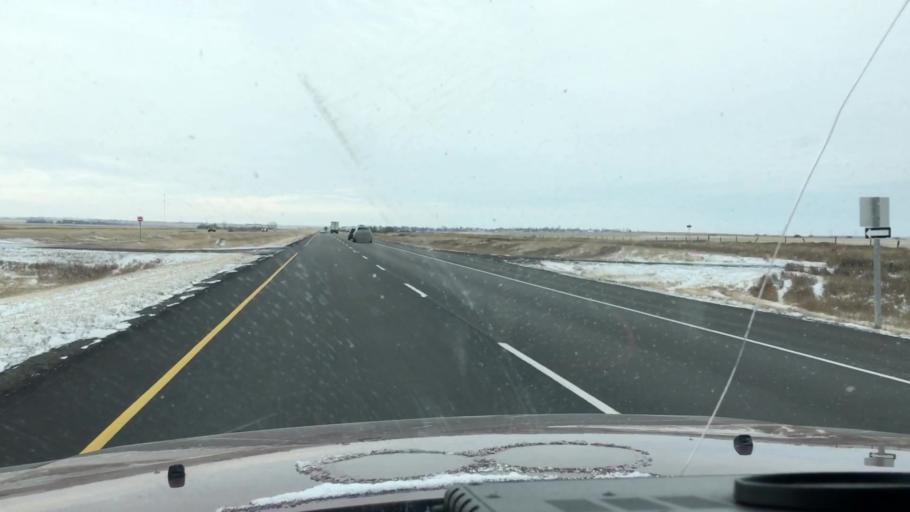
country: CA
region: Saskatchewan
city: Saskatoon
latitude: 51.8386
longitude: -106.5040
